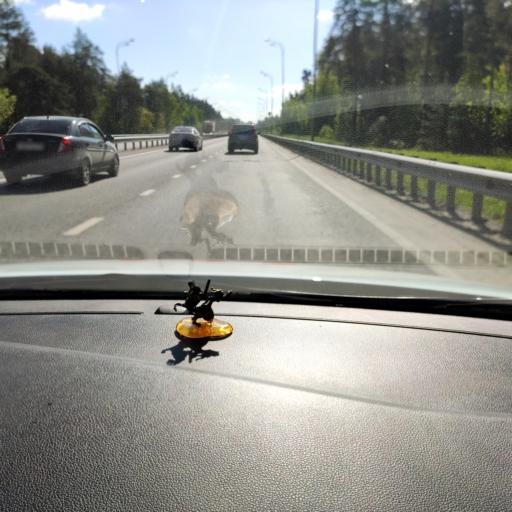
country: RU
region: Tatarstan
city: Staroye Arakchino
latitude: 55.8314
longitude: 49.0022
